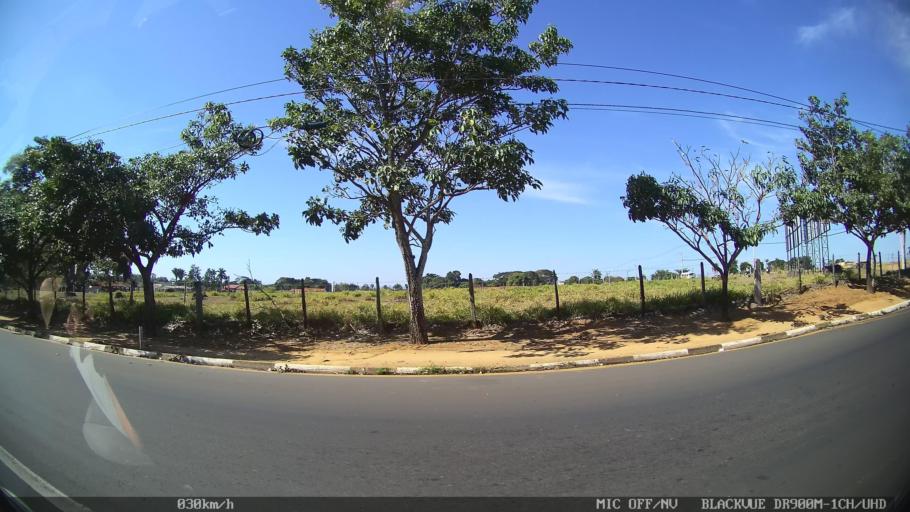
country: BR
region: Sao Paulo
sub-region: Franca
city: Franca
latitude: -20.4961
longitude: -47.3980
